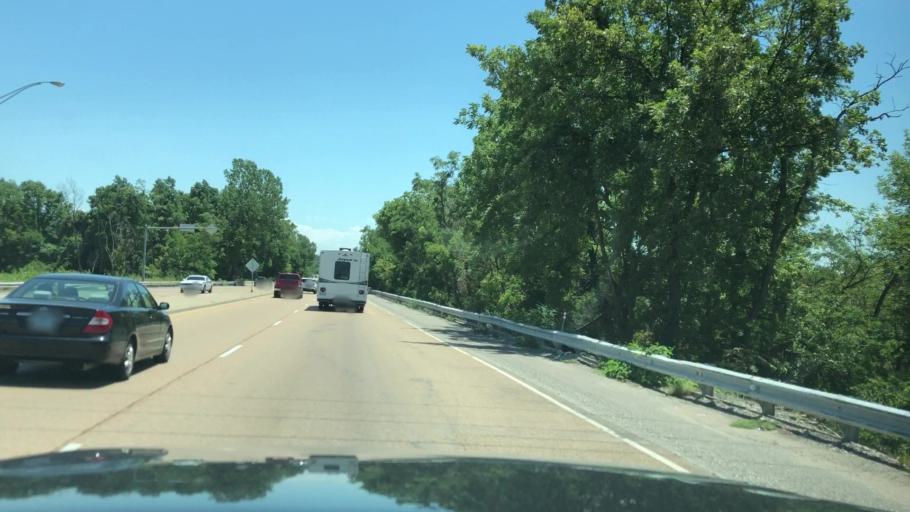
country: US
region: Illinois
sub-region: Saint Clair County
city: Alorton
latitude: 38.5606
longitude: -90.0839
